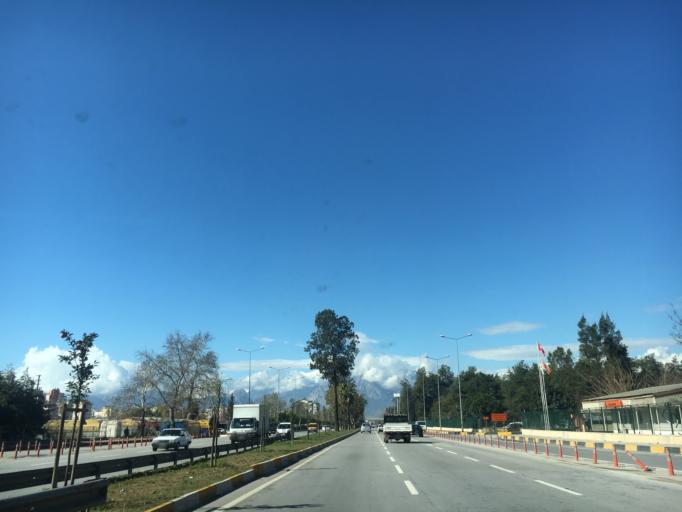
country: TR
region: Antalya
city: Antalya
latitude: 36.9052
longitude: 30.6783
